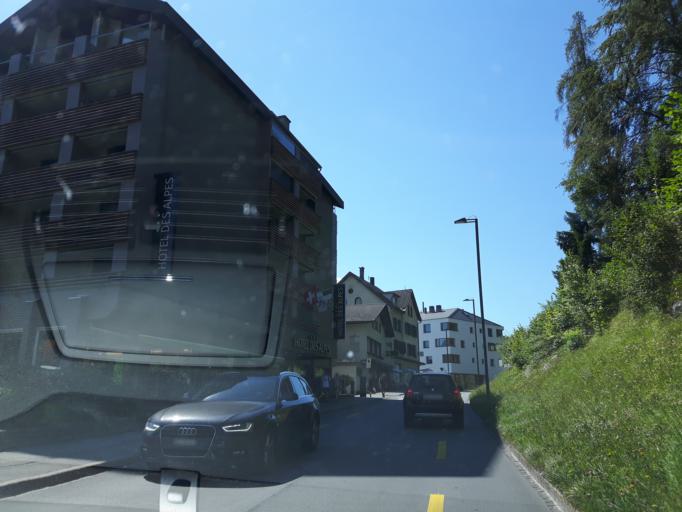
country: CH
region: Grisons
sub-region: Imboden District
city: Flims
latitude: 46.8267
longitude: 9.2885
